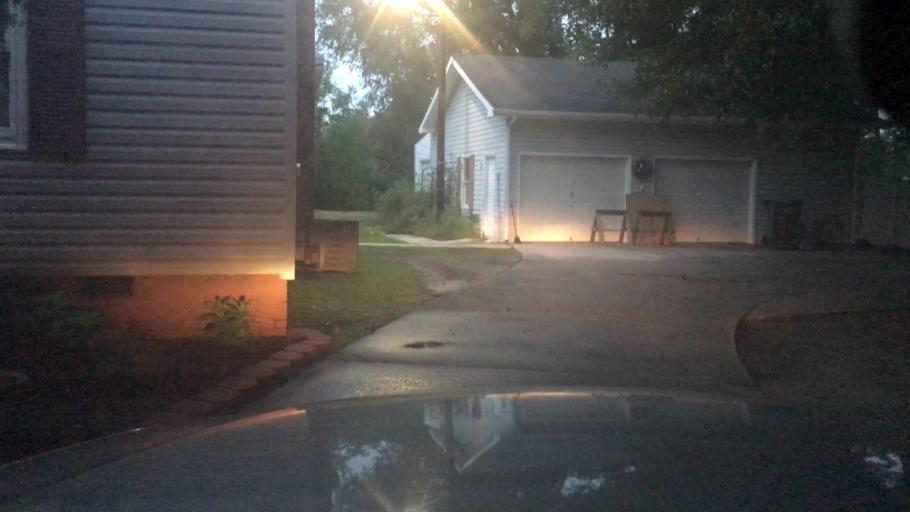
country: US
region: North Carolina
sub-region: Cumberland County
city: Hope Mills
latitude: 34.9582
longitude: -78.9378
